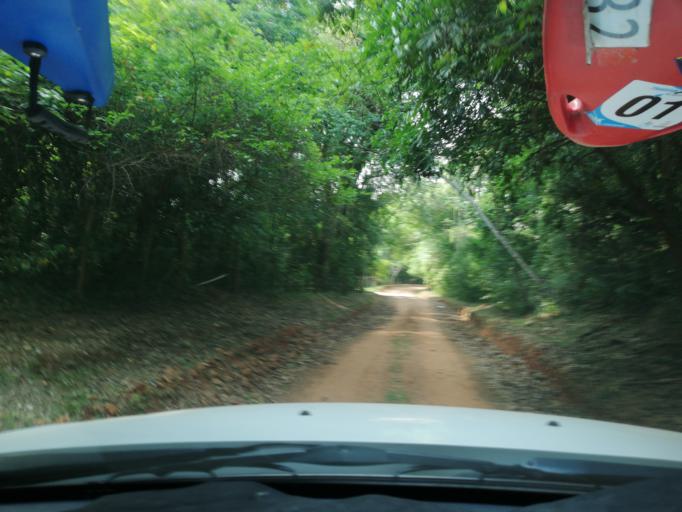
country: AR
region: Misiones
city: Santa Ana
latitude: -27.3028
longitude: -55.5795
